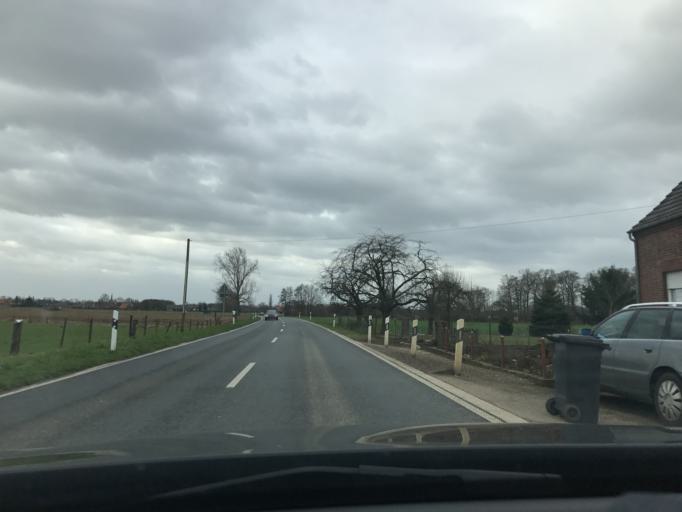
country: DE
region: North Rhine-Westphalia
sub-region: Regierungsbezirk Dusseldorf
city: Wachtendonk
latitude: 51.4234
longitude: 6.3471
